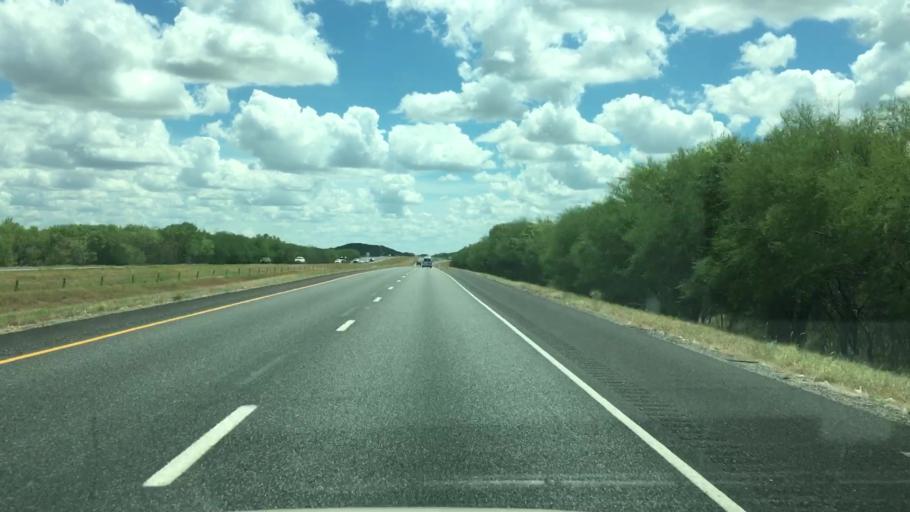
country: US
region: Texas
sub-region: Atascosa County
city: Pleasanton
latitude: 28.7421
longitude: -98.2923
